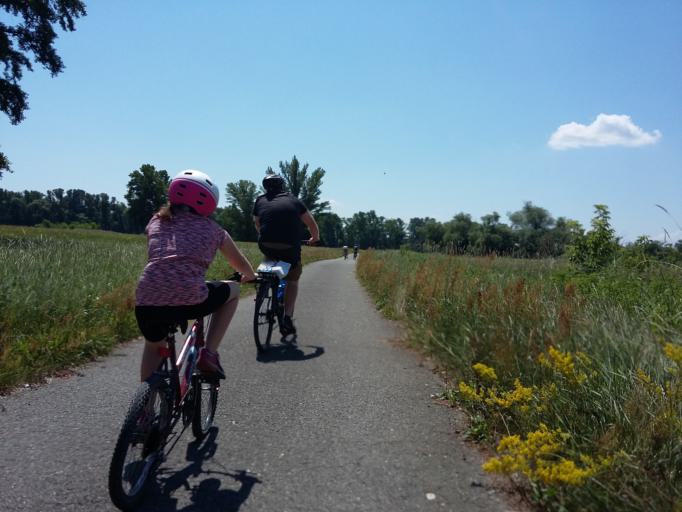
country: AT
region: Lower Austria
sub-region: Politischer Bezirk Ganserndorf
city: Marchegg
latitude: 48.2462
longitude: 16.9502
